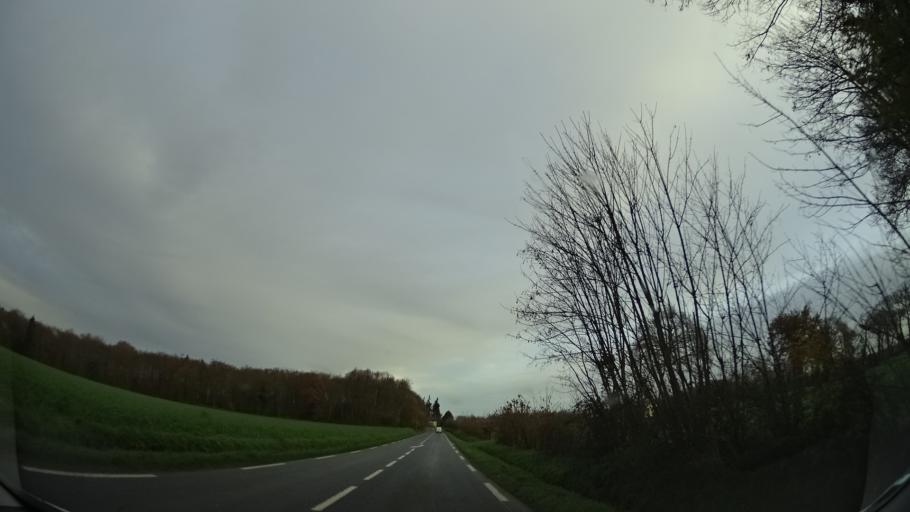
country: FR
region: Brittany
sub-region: Departement des Cotes-d'Armor
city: Evran
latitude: 48.3922
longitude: -1.9799
